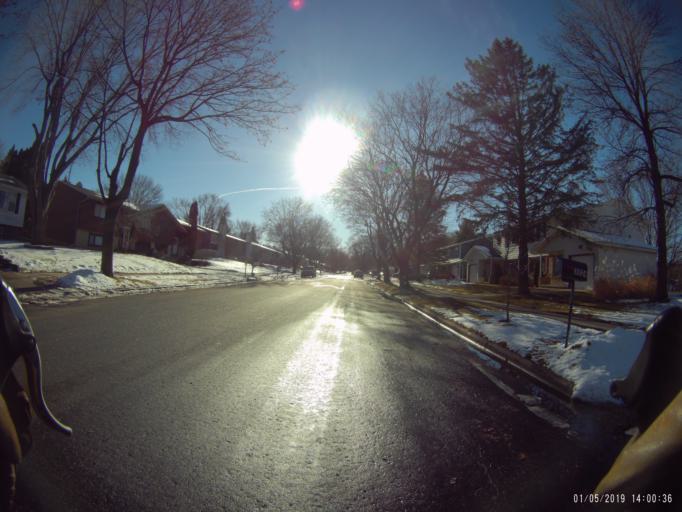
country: US
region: Wisconsin
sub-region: Dane County
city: Madison
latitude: 43.0302
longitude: -89.4220
